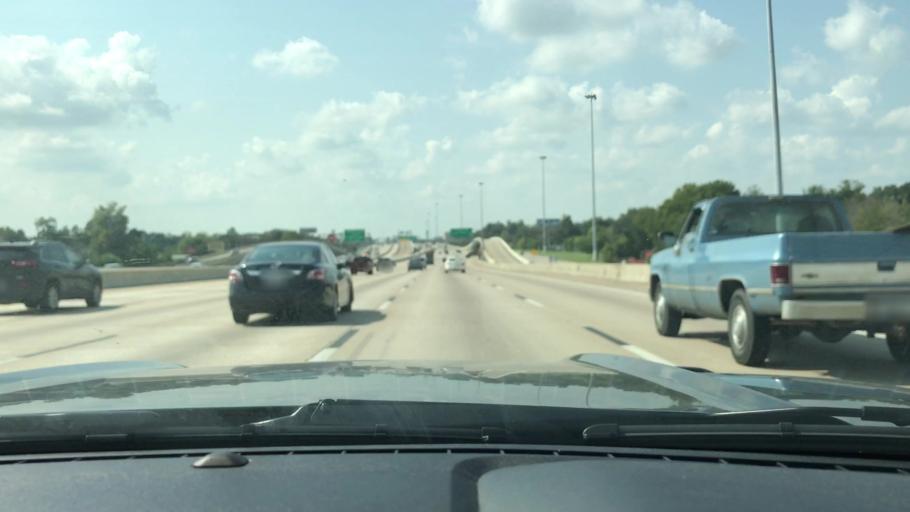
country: US
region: Texas
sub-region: Harris County
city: Aldine
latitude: 29.8582
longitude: -95.3337
